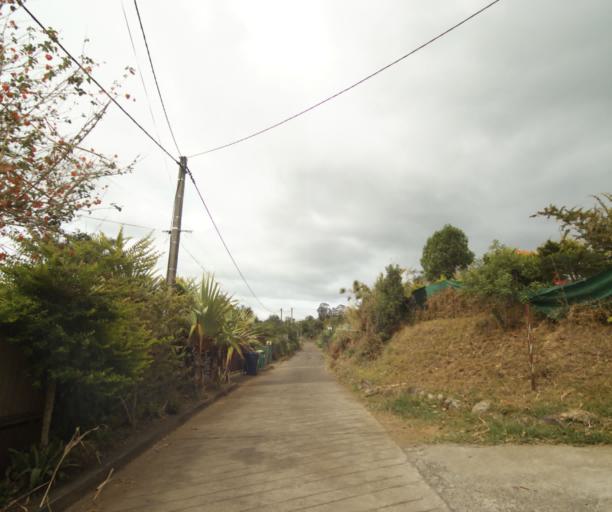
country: RE
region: Reunion
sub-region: Reunion
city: Saint-Paul
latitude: -21.0178
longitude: 55.3280
